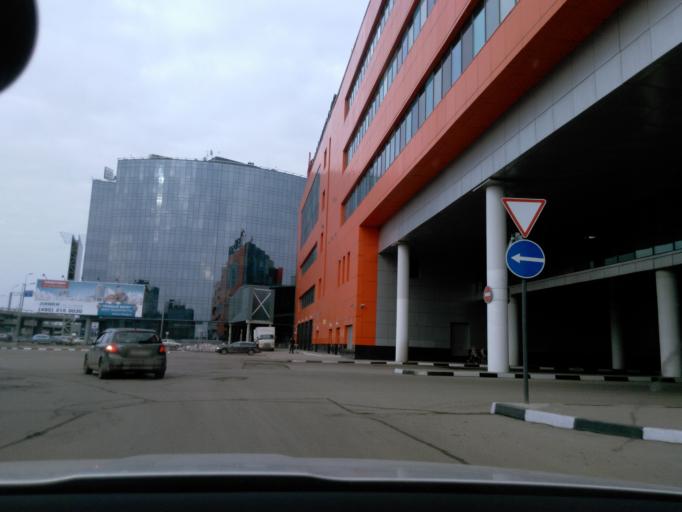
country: RU
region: Moscow
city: Khimki
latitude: 55.9636
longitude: 37.4158
